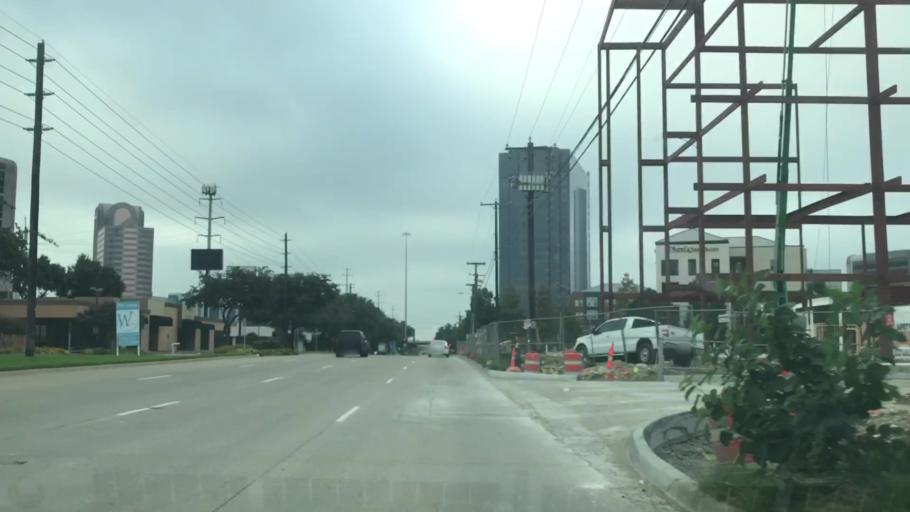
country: US
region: Texas
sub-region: Dallas County
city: Addison
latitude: 32.9319
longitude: -96.8228
